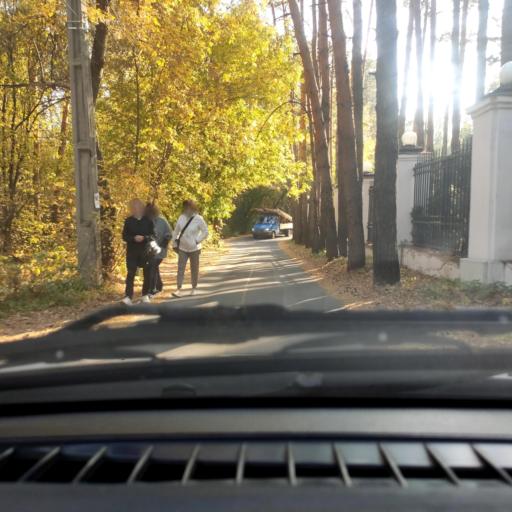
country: RU
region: Samara
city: Tol'yatti
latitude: 53.4770
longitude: 49.3579
